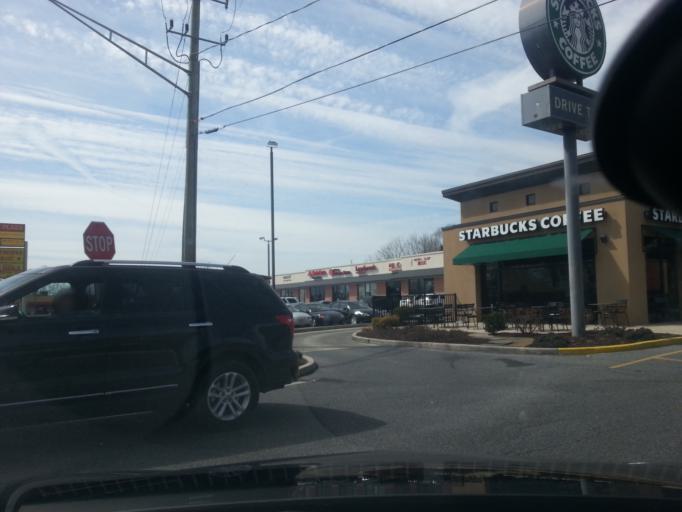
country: US
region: Maryland
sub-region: Wicomico County
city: Delmar
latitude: 38.4054
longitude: -75.5684
